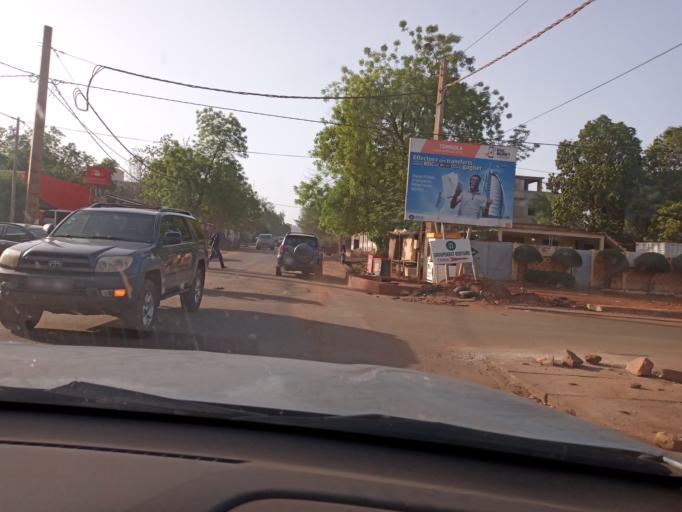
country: ML
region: Bamako
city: Bamako
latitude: 12.6611
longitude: -7.9723
